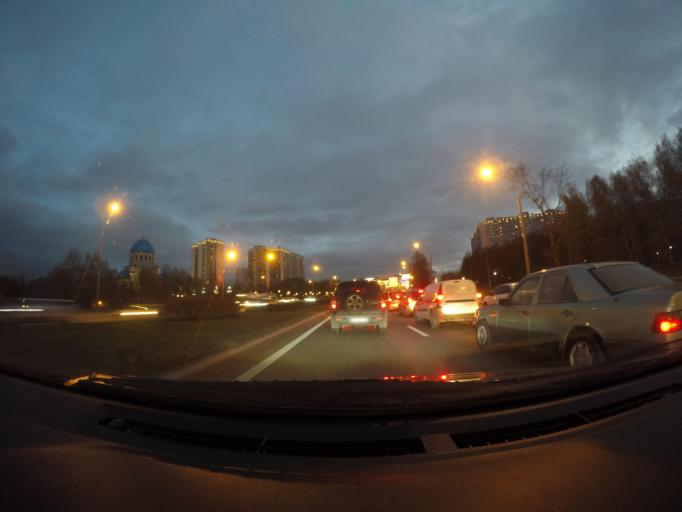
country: RU
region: Moskovskaya
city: Kur'yanovo
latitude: 55.6281
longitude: 37.7083
